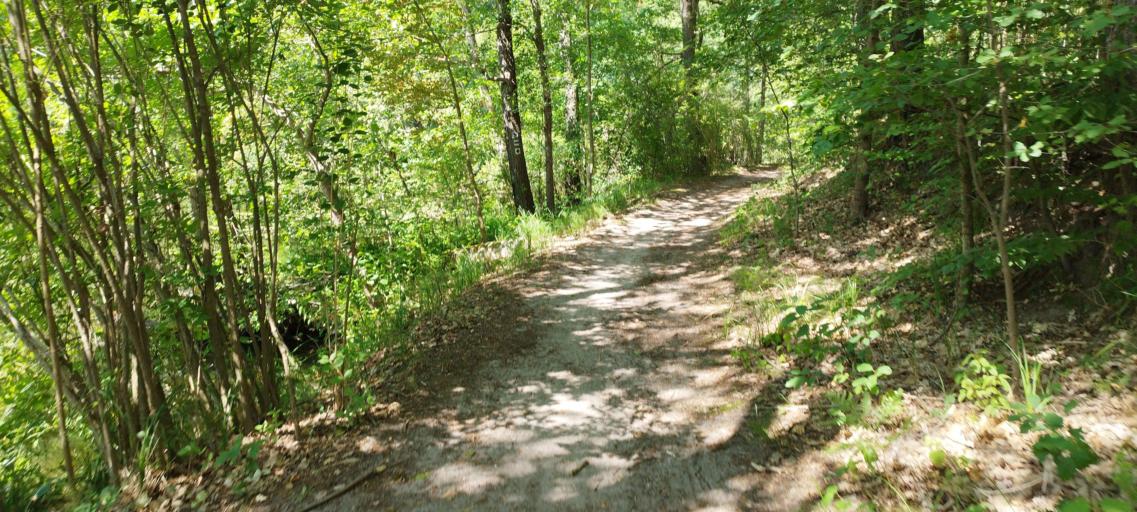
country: DE
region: Brandenburg
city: Mixdorf
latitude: 52.1799
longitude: 14.4298
